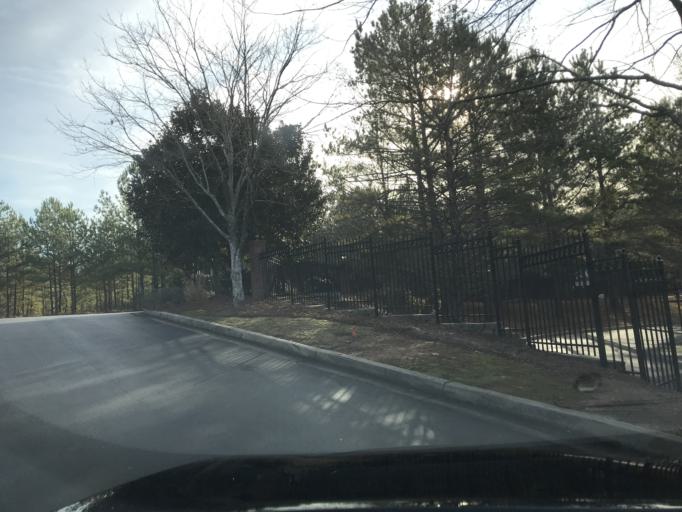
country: US
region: Georgia
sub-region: Clayton County
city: Morrow
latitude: 33.5544
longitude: -84.3522
